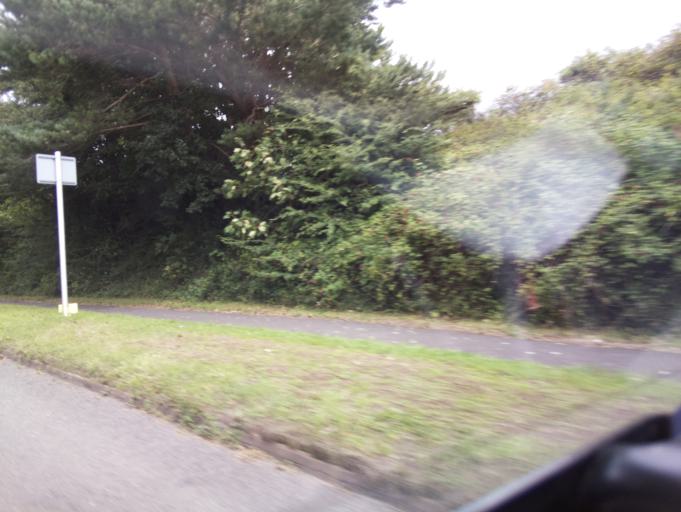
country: GB
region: England
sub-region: Devon
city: Dawlish
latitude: 50.5659
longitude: -3.4763
